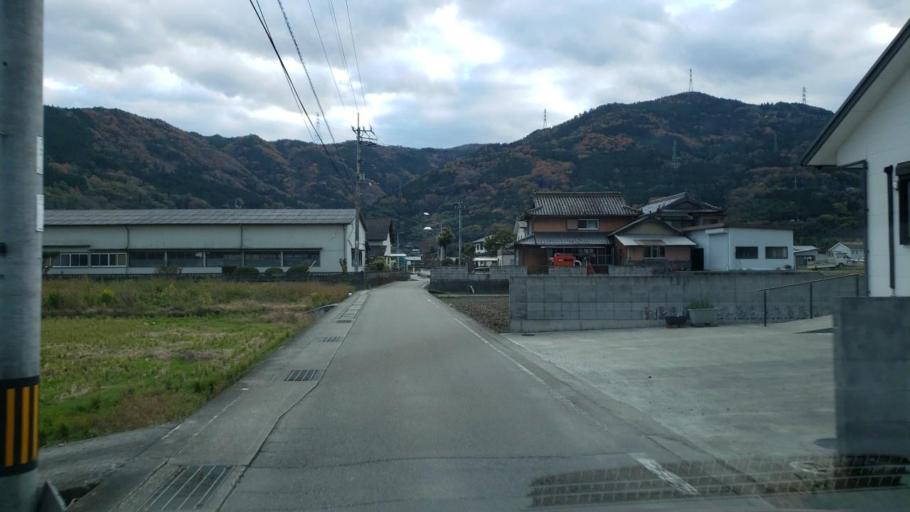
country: JP
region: Tokushima
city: Wakimachi
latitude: 34.0612
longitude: 134.1436
